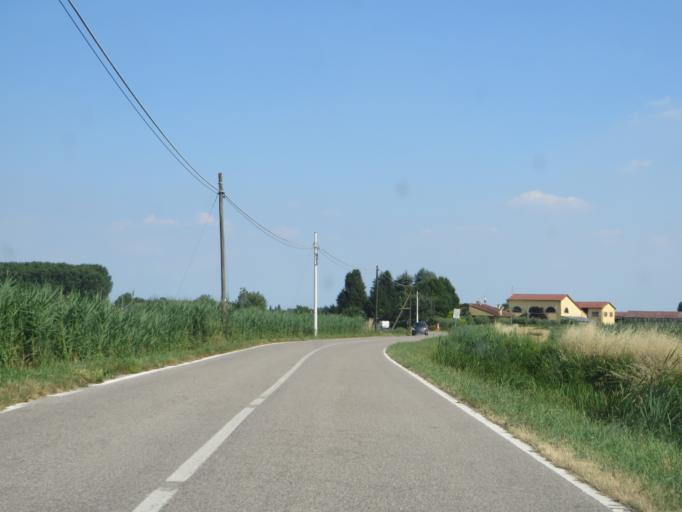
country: IT
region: Veneto
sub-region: Provincia di Verona
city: Angiari
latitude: 45.2270
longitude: 11.2593
